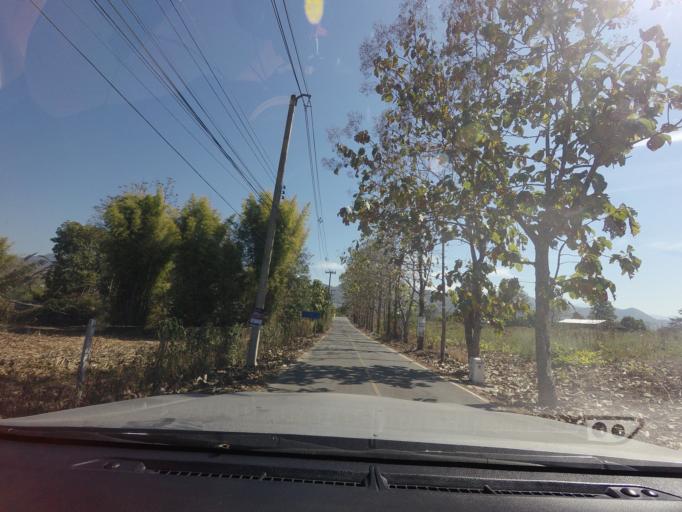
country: TH
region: Mae Hong Son
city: Wiang Nuea
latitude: 19.3862
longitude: 98.4358
